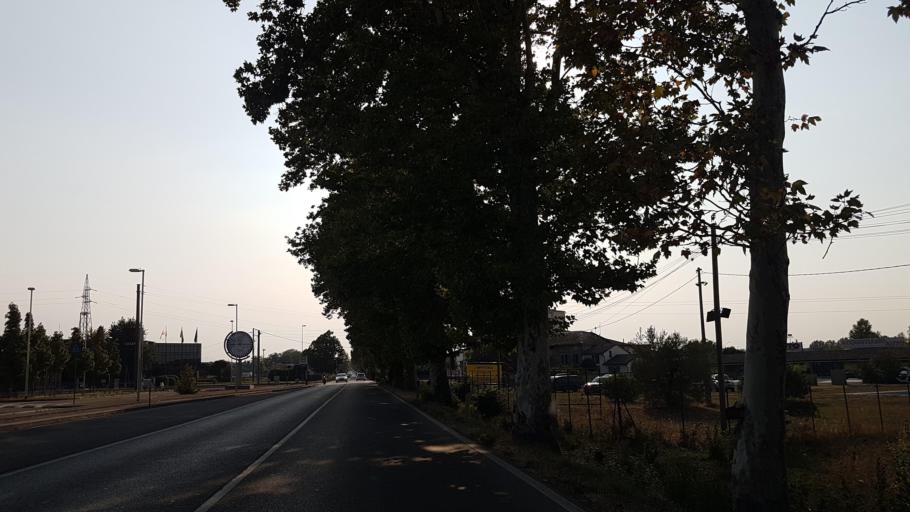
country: IT
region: Emilia-Romagna
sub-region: Provincia di Parma
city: Vicofertile
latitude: 44.7743
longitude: 10.2712
